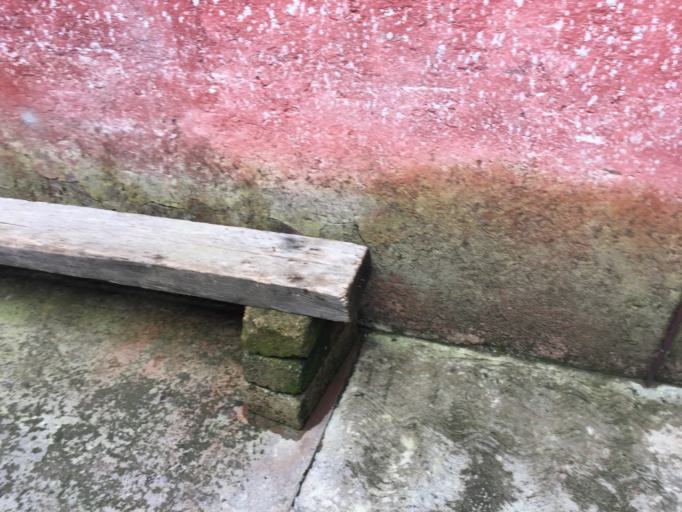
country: MX
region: Mexico
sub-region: Ocuilan
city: Plaza Nueva
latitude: 18.9237
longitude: -99.4382
